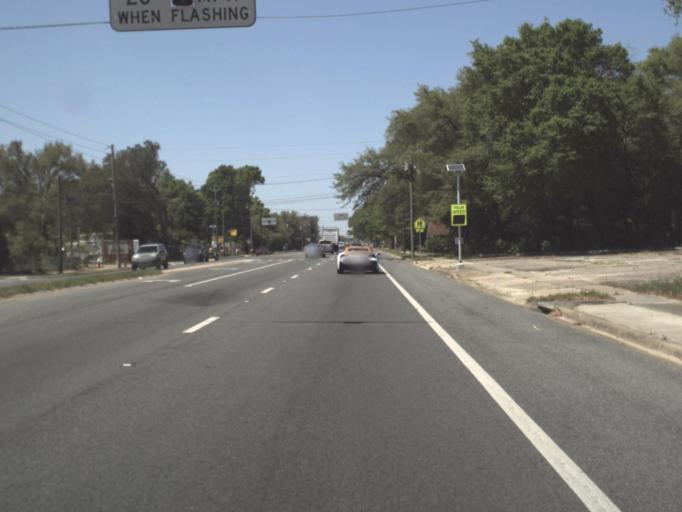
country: US
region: Florida
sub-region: Escambia County
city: Bellview
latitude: 30.4640
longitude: -87.3023
